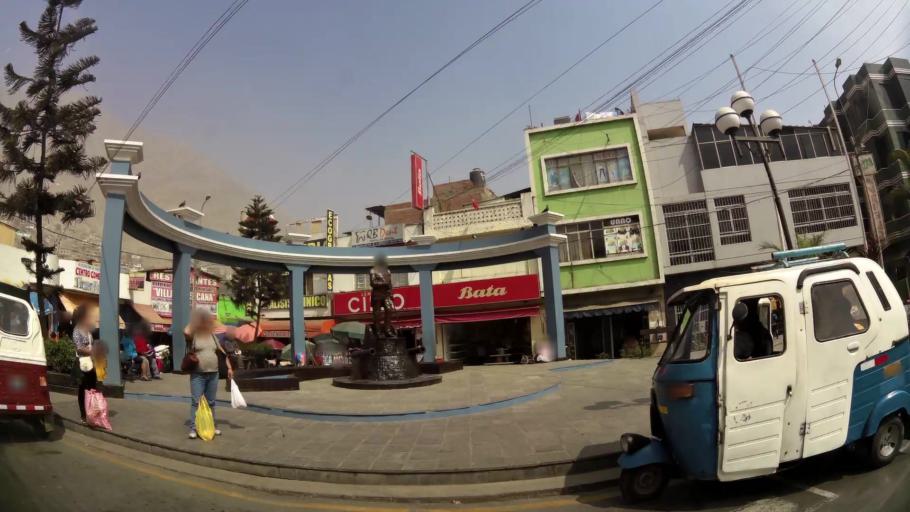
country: PE
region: Lima
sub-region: Lima
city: Asentamiento Humano Nicolas de Pierola
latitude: -11.9350
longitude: -76.6929
